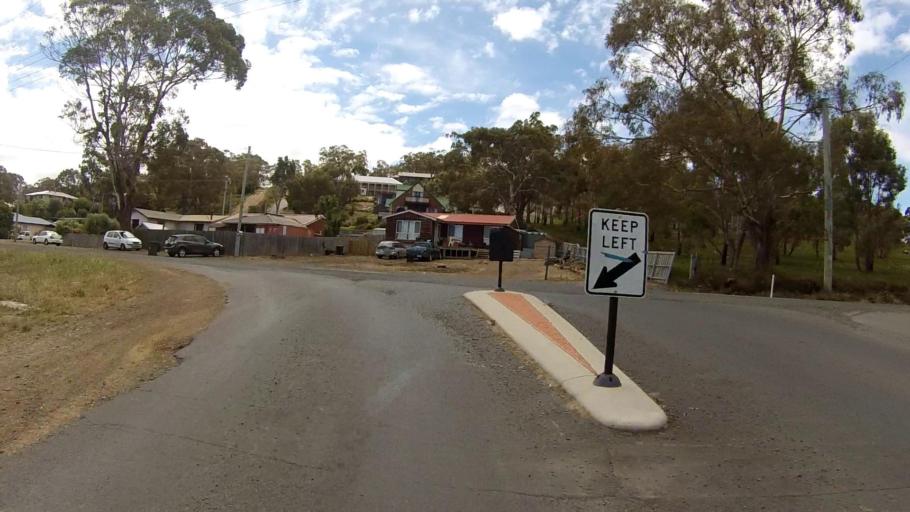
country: AU
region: Tasmania
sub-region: Sorell
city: Sorell
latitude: -42.8669
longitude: 147.6449
